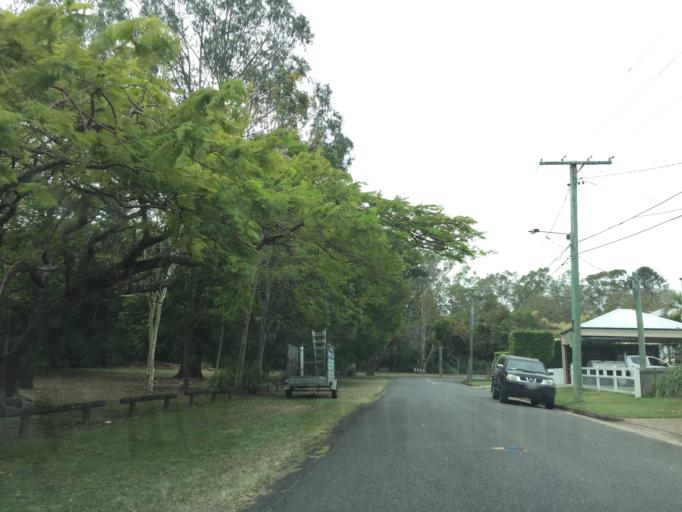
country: AU
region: Queensland
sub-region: Brisbane
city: Milton
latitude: -27.4458
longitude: 152.9750
